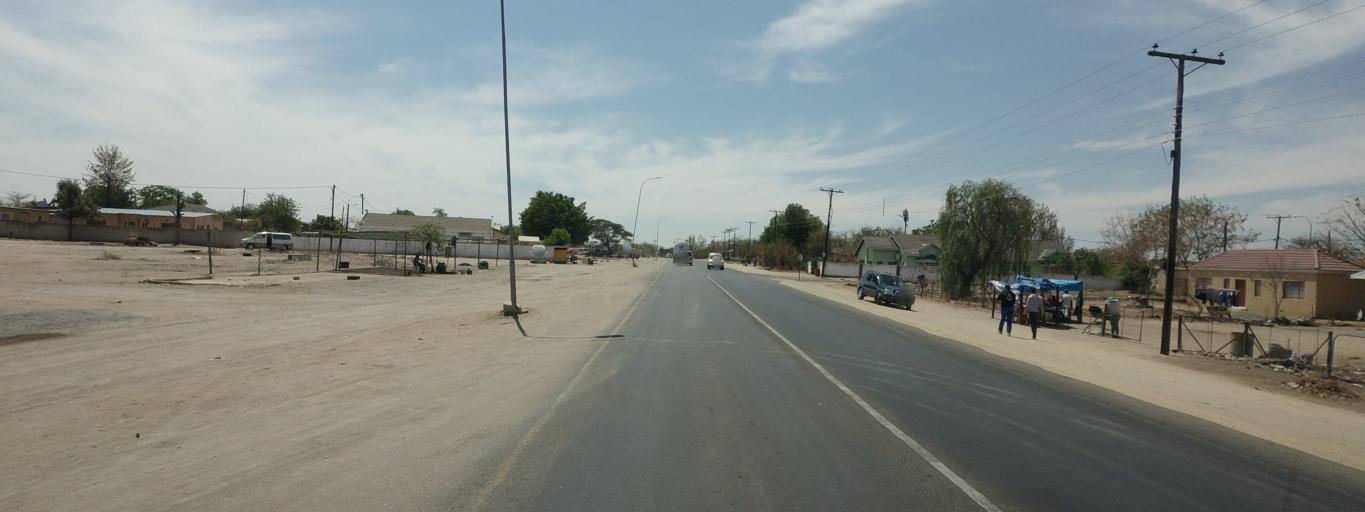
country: BW
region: North East
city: Francistown
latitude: -21.1665
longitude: 27.4947
